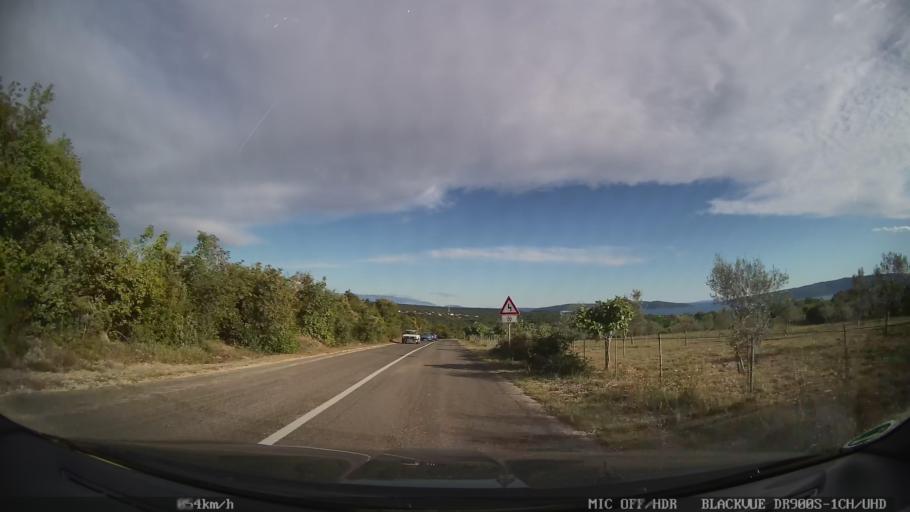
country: HR
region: Primorsko-Goranska
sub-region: Grad Krk
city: Krk
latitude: 45.0626
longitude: 14.4767
